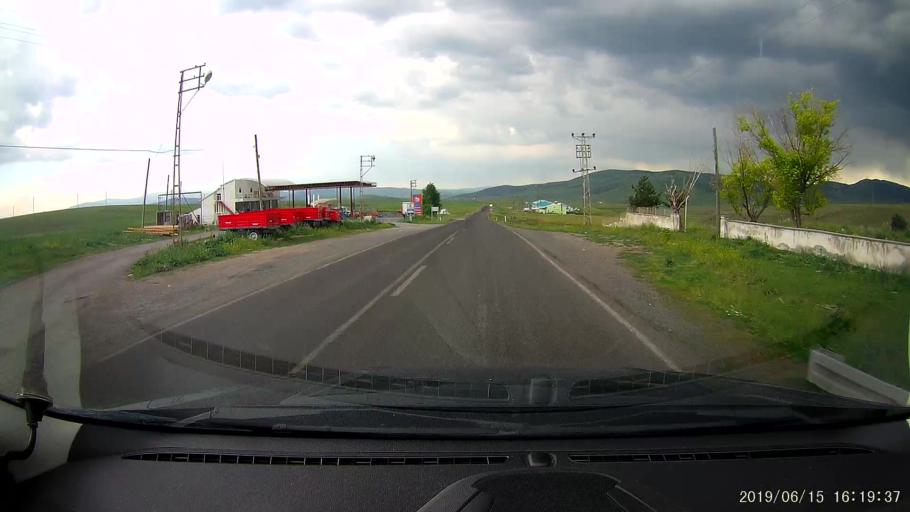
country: TR
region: Ardahan
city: Hanak
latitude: 41.2265
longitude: 42.8498
